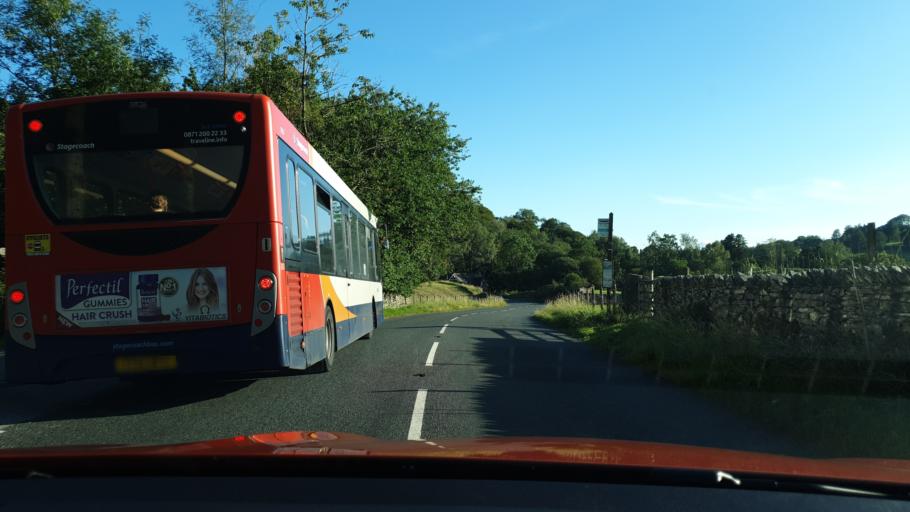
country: GB
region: England
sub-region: Cumbria
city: Windermere
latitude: 54.4190
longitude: -2.9045
